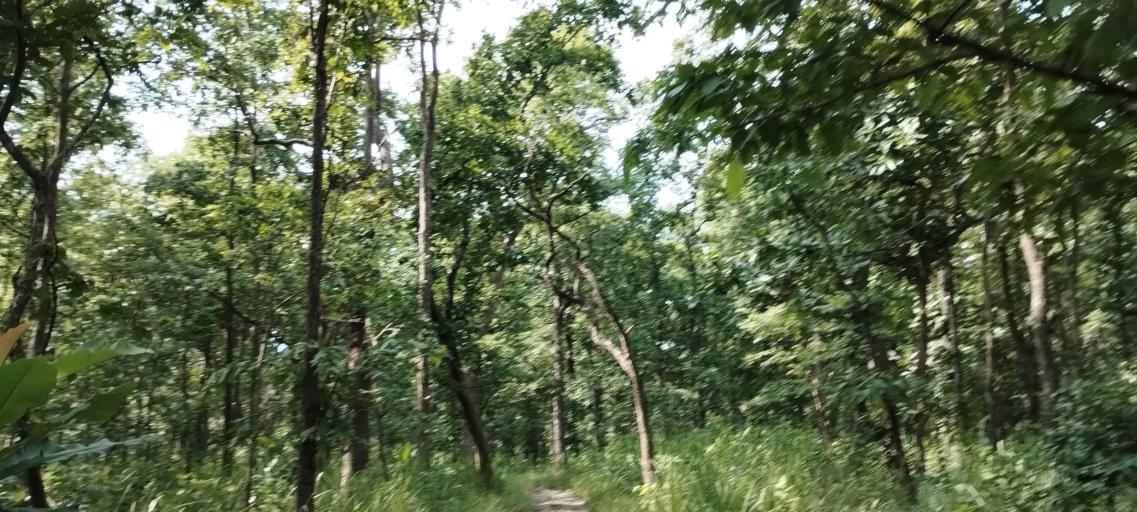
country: NP
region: Far Western
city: Tikapur
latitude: 28.5657
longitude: 81.2929
